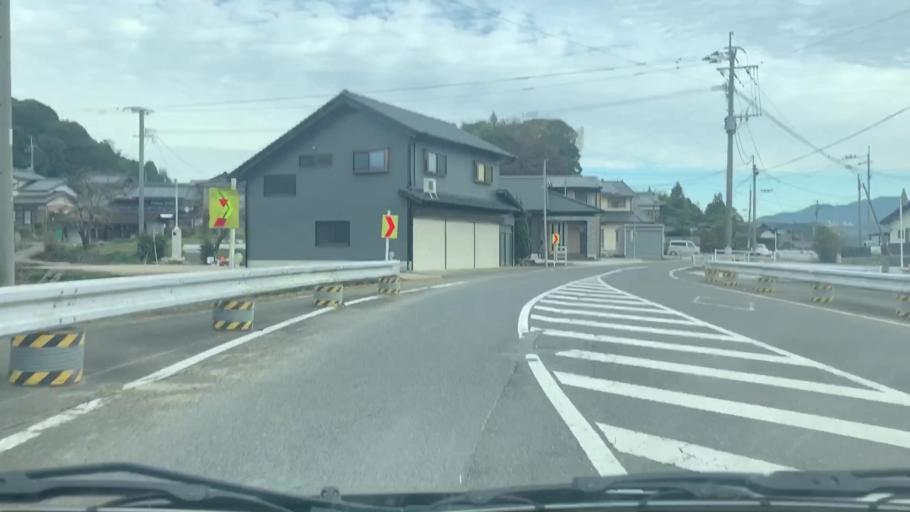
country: JP
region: Saga Prefecture
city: Takeocho-takeo
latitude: 33.2008
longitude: 129.9607
